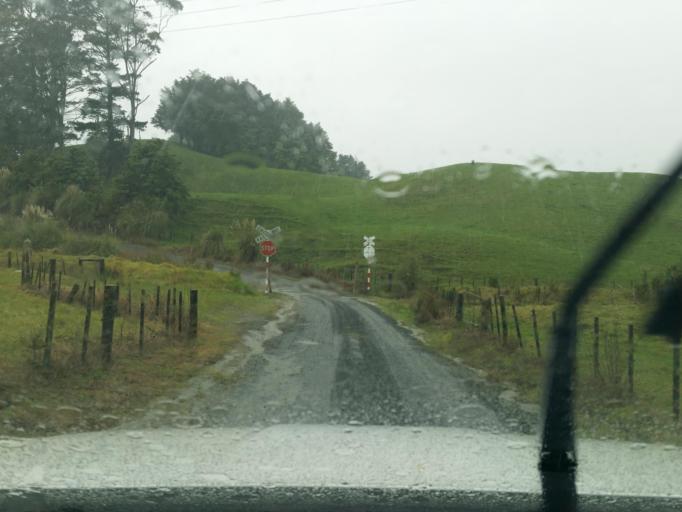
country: NZ
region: Northland
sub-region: Kaipara District
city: Dargaville
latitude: -35.8650
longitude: 174.0151
